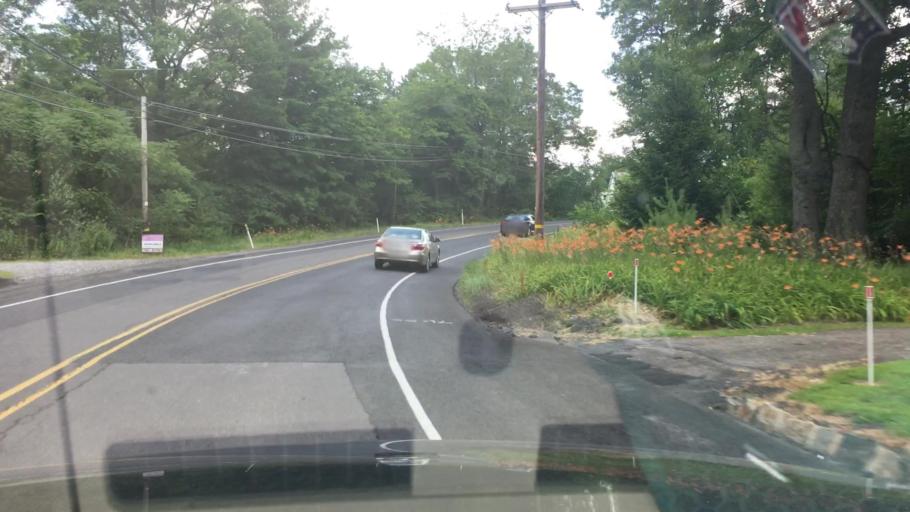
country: US
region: Pennsylvania
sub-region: Schuylkill County
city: Minersville
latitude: 40.7044
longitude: -76.3281
